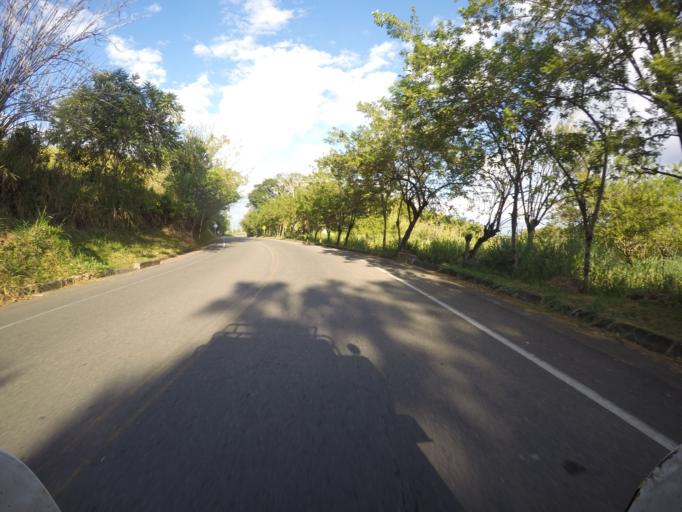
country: CO
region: Valle del Cauca
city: Alcala
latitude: 4.6943
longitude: -75.8266
